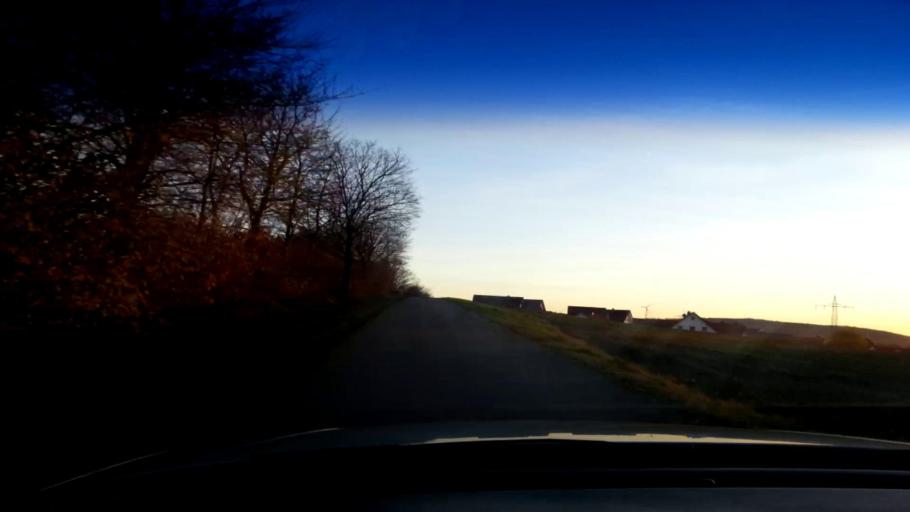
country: DE
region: Bavaria
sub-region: Upper Franconia
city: Zapfendorf
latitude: 50.0249
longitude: 10.9437
